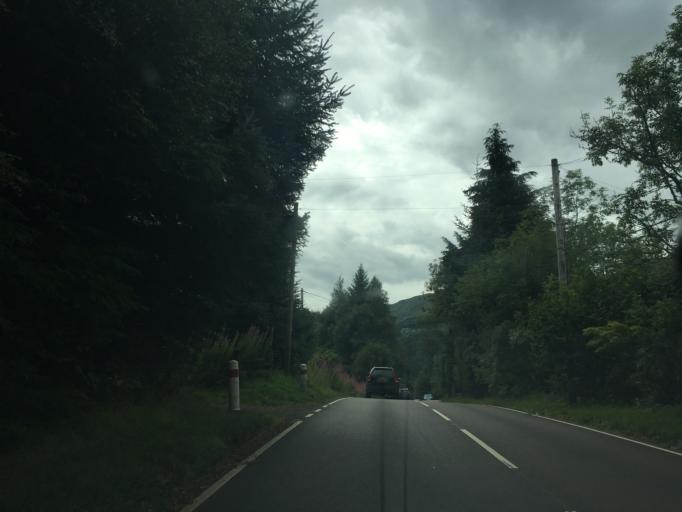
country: GB
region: Scotland
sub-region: Stirling
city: Callander
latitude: 56.3203
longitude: -4.3283
